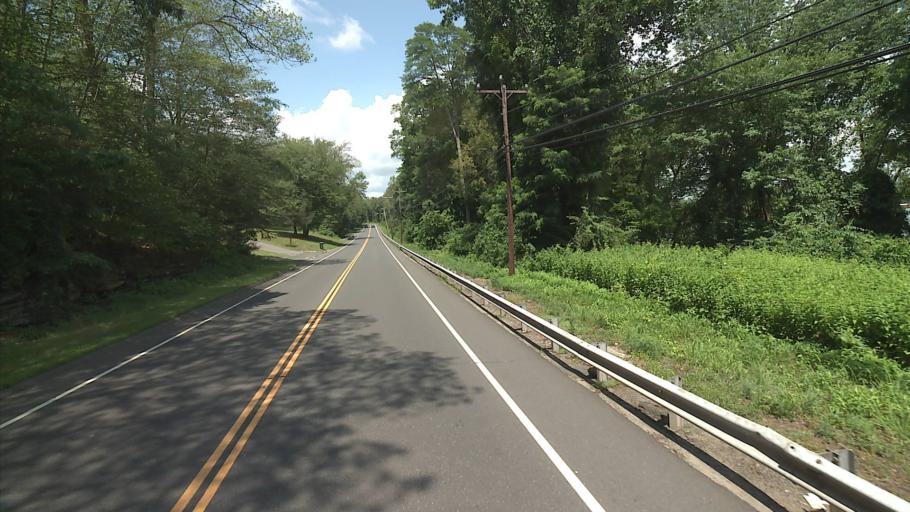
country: US
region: Connecticut
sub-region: Middlesex County
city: East Haddam
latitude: 41.4390
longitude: -72.4634
